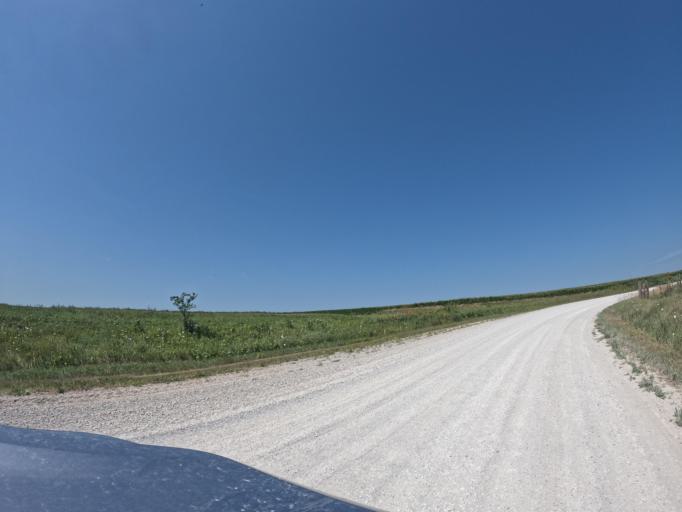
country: US
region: Iowa
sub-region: Henry County
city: Mount Pleasant
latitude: 40.8866
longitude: -91.5687
